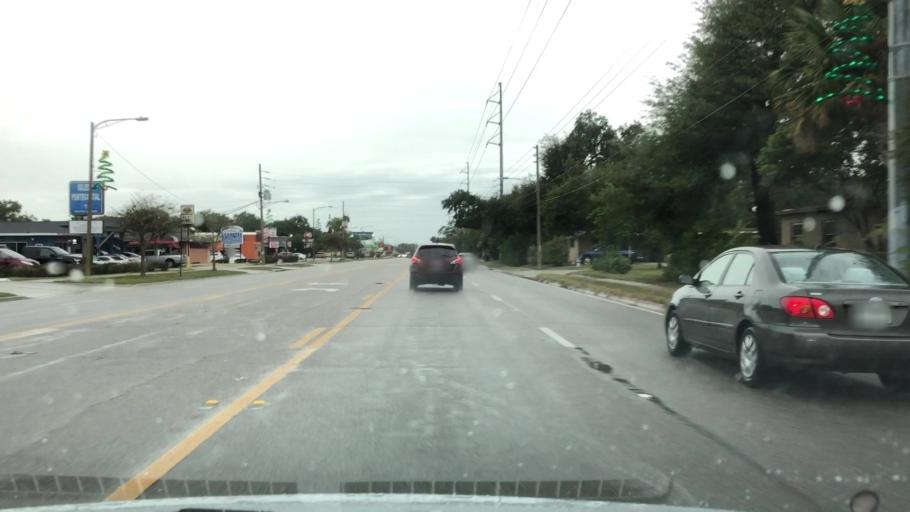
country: US
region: Florida
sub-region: Orange County
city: Conway
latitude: 28.5243
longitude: -81.3353
